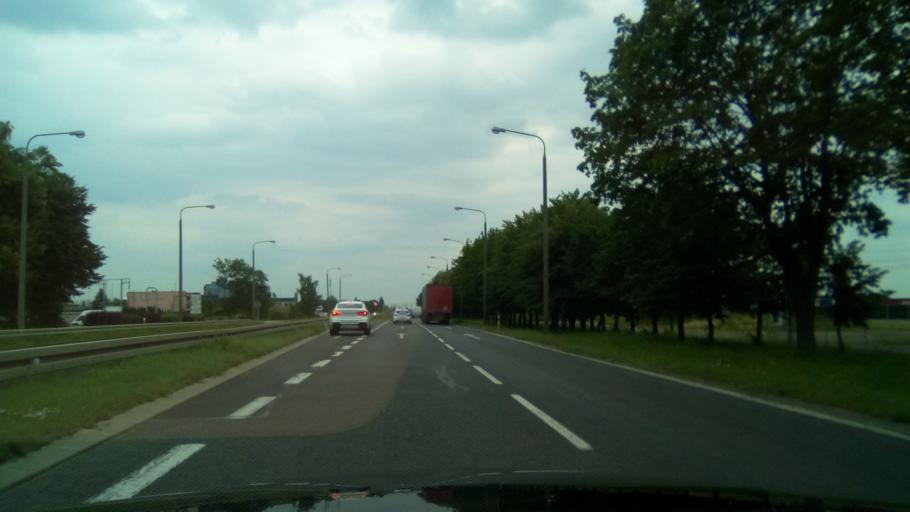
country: PL
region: Greater Poland Voivodeship
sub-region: Powiat poznanski
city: Swarzedz
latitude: 52.3997
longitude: 17.1367
